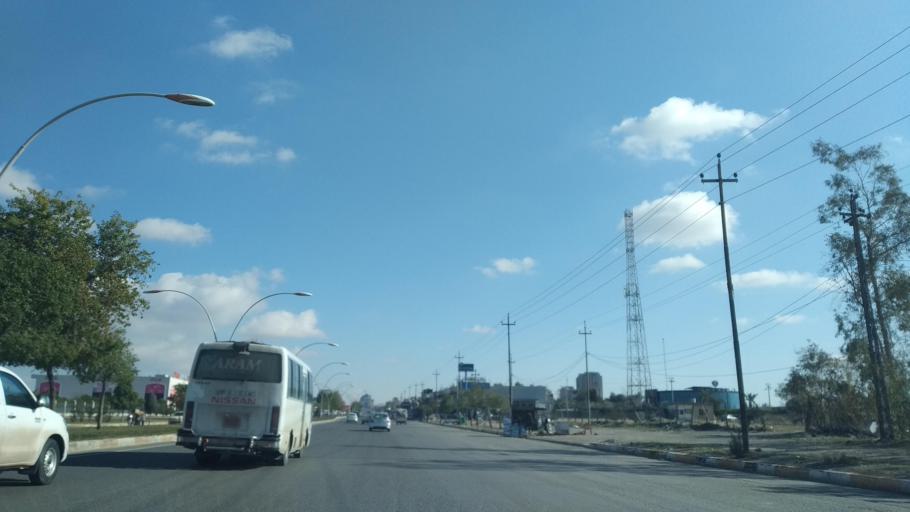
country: IQ
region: Arbil
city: Erbil
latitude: 36.2006
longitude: 44.0925
